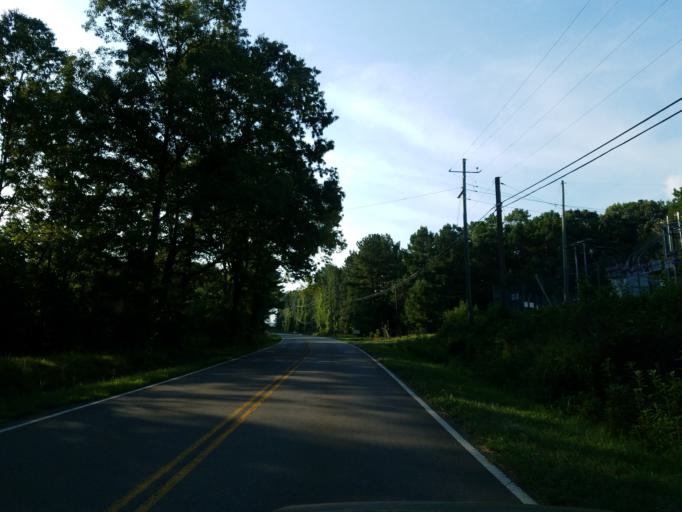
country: US
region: Georgia
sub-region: Pickens County
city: Jasper
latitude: 34.5321
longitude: -84.5300
